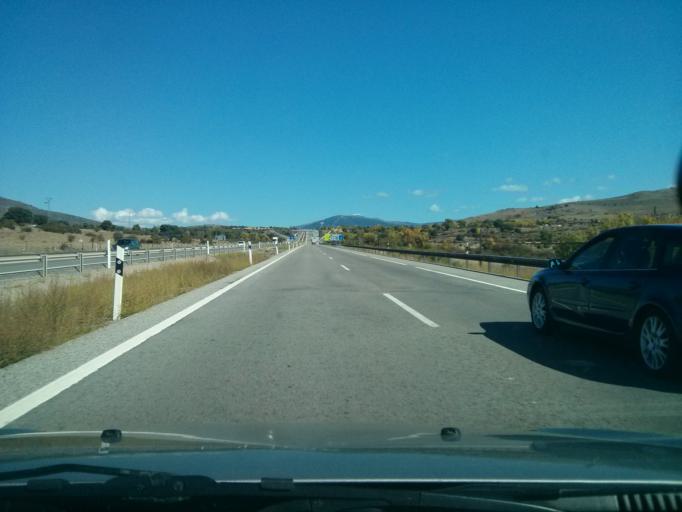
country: ES
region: Madrid
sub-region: Provincia de Madrid
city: Gascones
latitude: 41.0187
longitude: -3.6274
